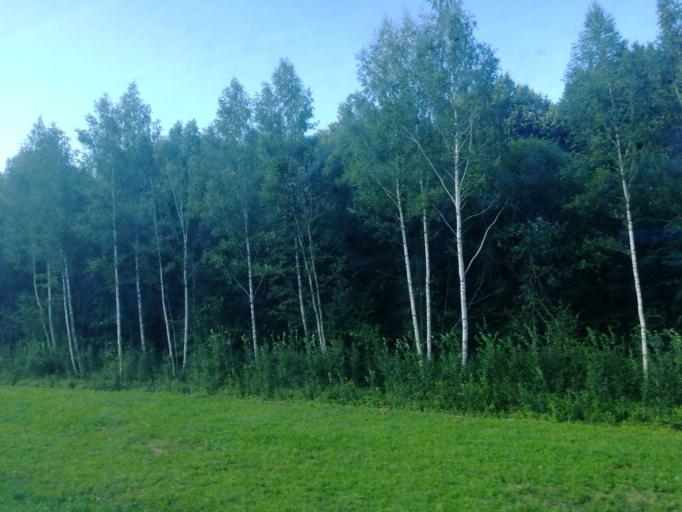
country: RU
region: Tula
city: Leninskiy
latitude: 54.2350
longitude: 37.3543
